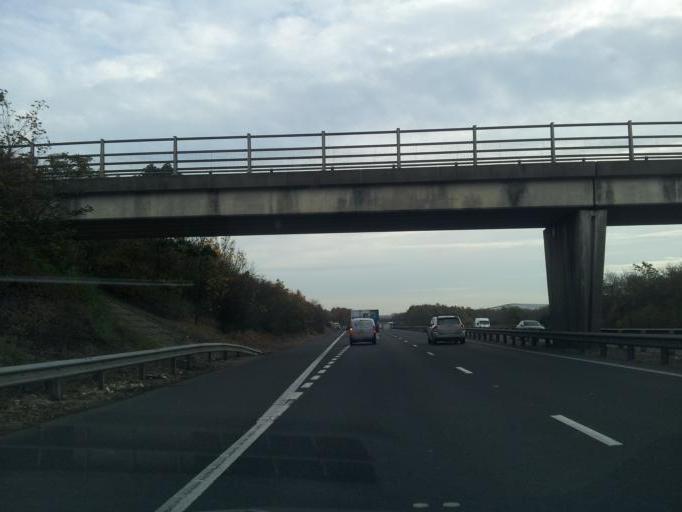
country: GB
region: England
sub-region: Cambridgeshire
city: Duxford
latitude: 52.1029
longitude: 0.1344
